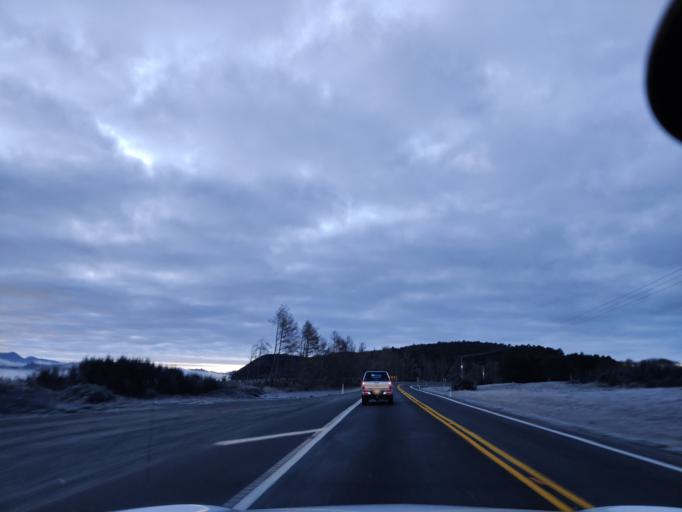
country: NZ
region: Waikato
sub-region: South Waikato District
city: Tokoroa
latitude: -38.4005
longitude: 176.0486
